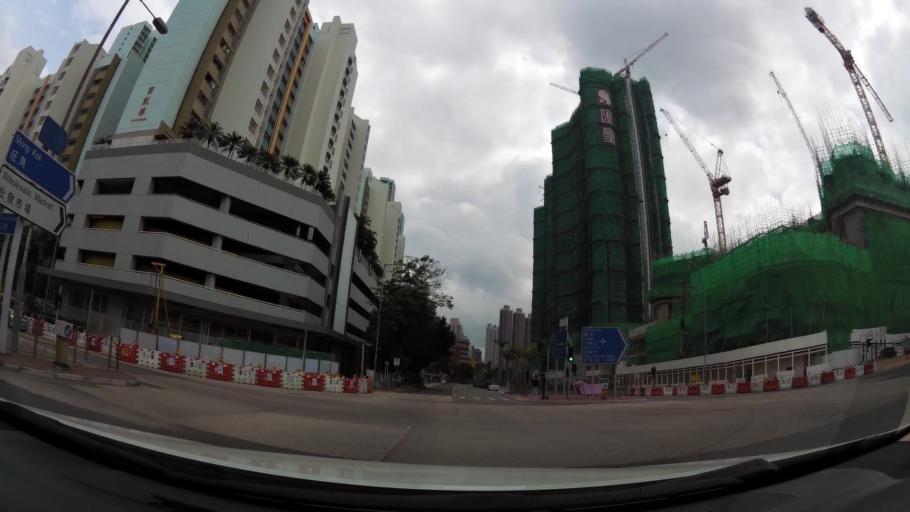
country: HK
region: Sham Shui Po
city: Sham Shui Po
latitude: 22.3291
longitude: 114.1527
